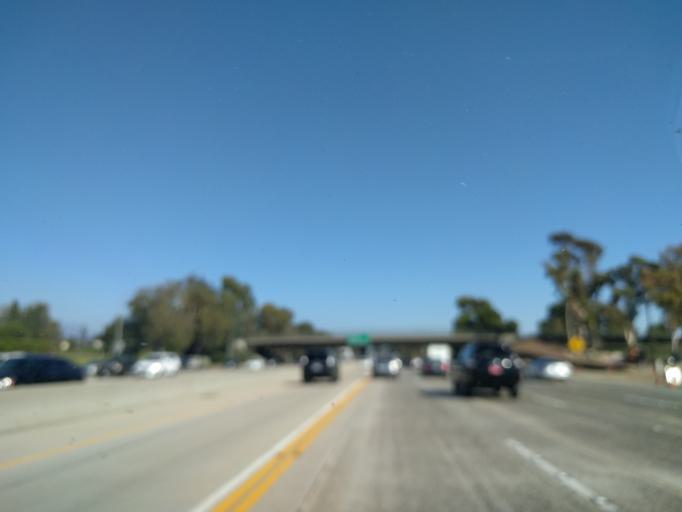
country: US
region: California
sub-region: Orange County
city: Irvine
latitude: 33.6699
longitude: -117.8247
